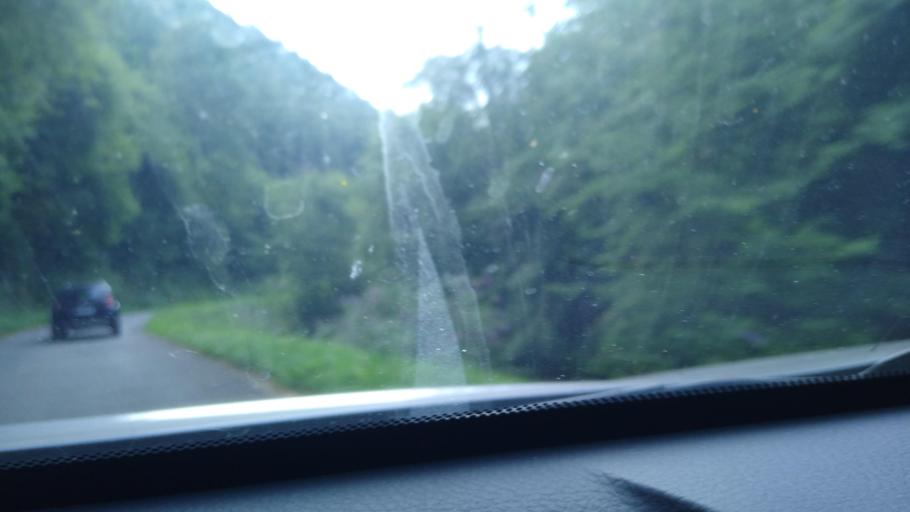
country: FR
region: Midi-Pyrenees
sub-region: Departement de l'Ariege
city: Saint-Girons
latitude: 42.8053
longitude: 1.1947
